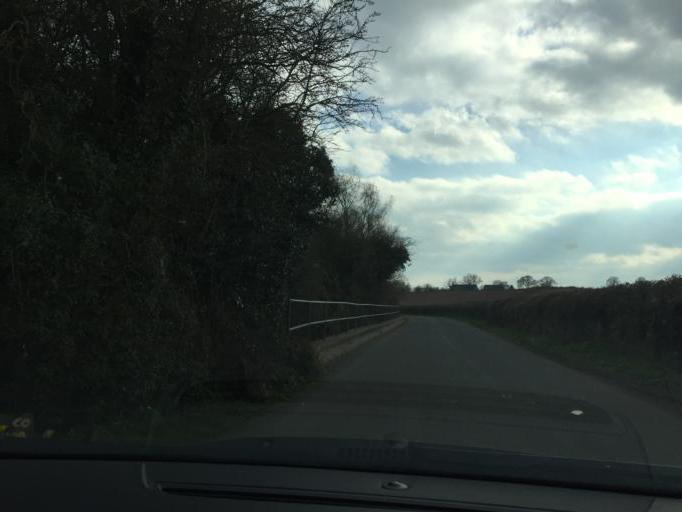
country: GB
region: England
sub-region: Coventry
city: Keresley
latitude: 52.4343
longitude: -1.5705
